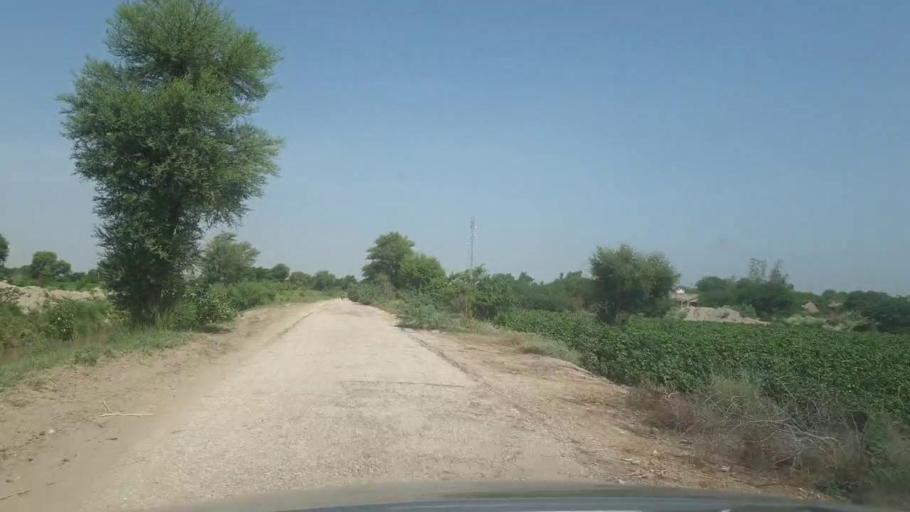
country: PK
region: Sindh
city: Khairpur
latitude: 27.4019
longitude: 69.0372
